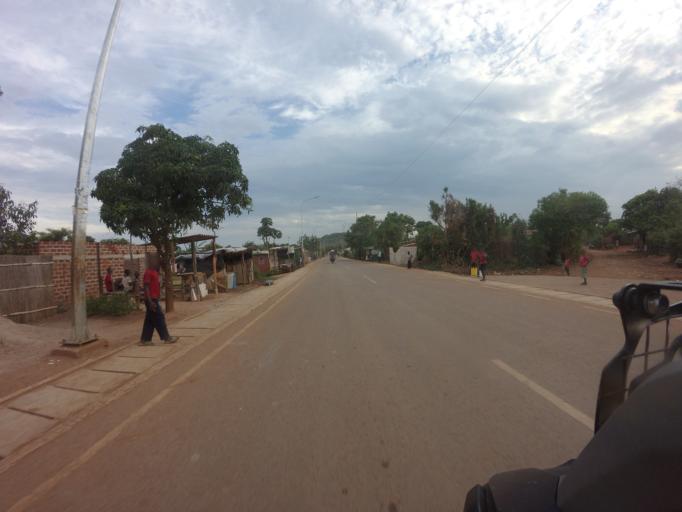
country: ZM
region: Lusaka
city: Lusaka
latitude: -15.5344
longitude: 28.2372
